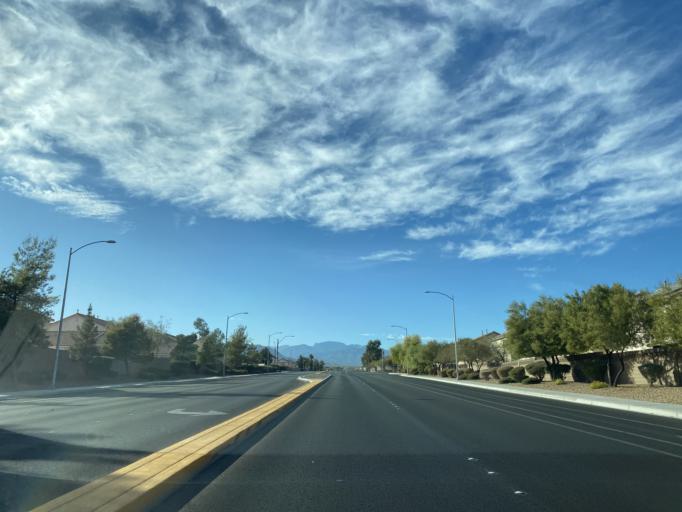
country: US
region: Nevada
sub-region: Clark County
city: Summerlin South
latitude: 36.3066
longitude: -115.2855
